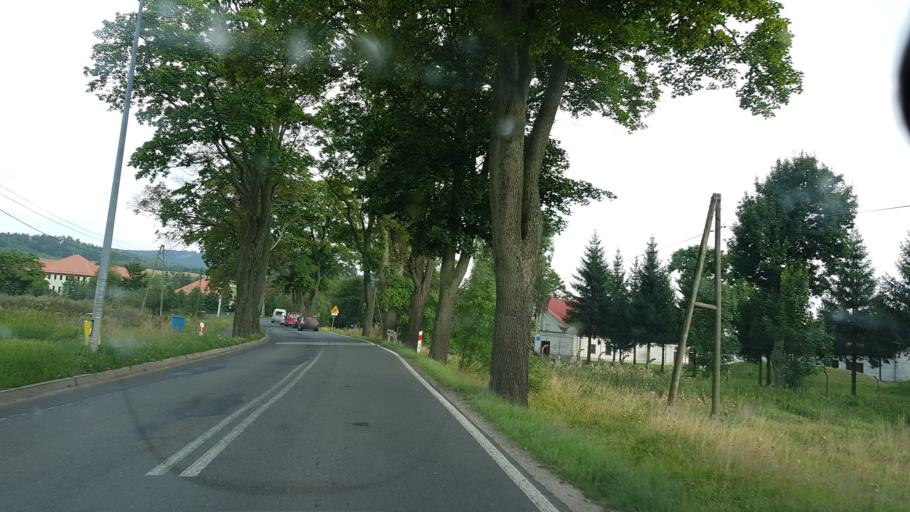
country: PL
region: Lower Silesian Voivodeship
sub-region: Powiat kamiennogorski
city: Marciszow
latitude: 50.8512
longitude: 16.0122
